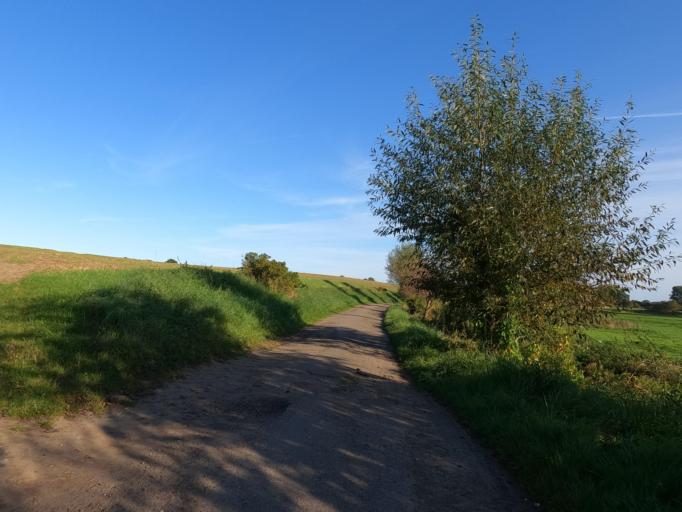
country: DE
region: Schleswig-Holstein
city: Neukirchen
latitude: 54.3133
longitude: 11.0257
